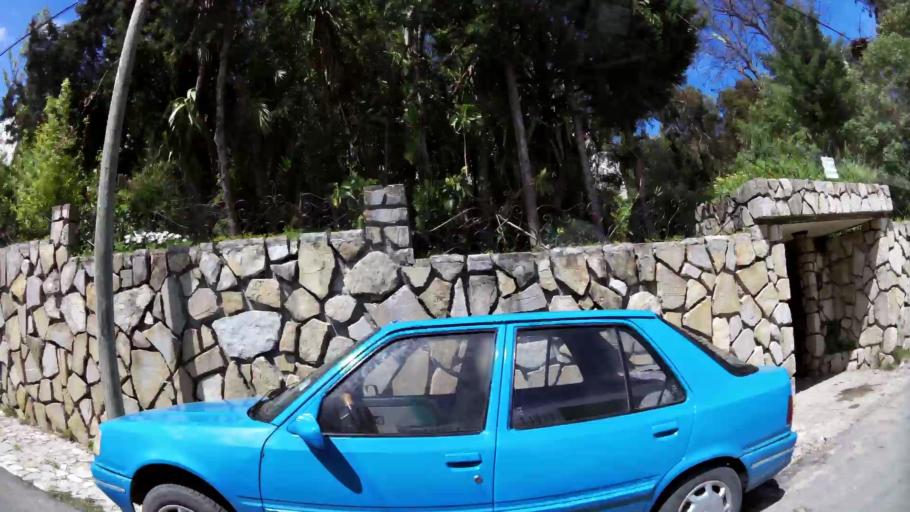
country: MA
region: Tanger-Tetouan
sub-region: Tanger-Assilah
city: Tangier
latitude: 35.7894
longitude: -5.8433
